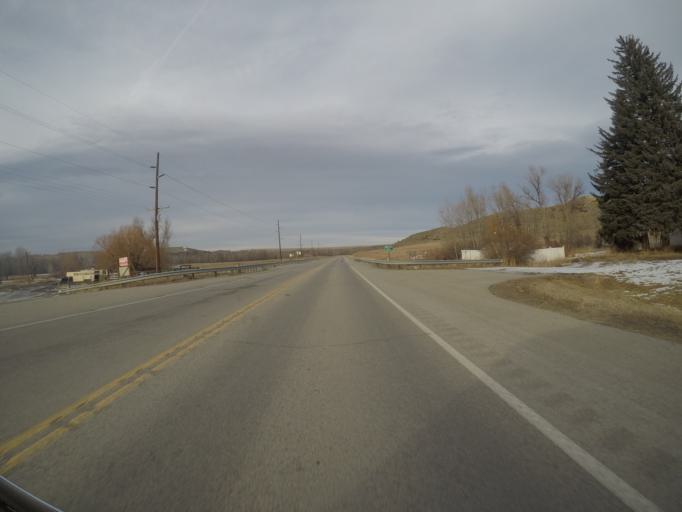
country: US
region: Montana
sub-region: Stillwater County
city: Absarokee
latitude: 45.4829
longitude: -109.4514
